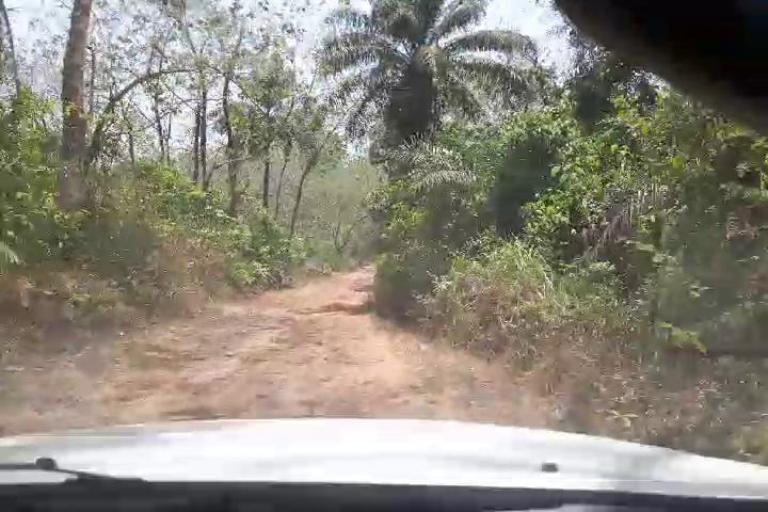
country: SL
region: Northern Province
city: Alikalia
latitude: 9.0696
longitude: -11.4832
